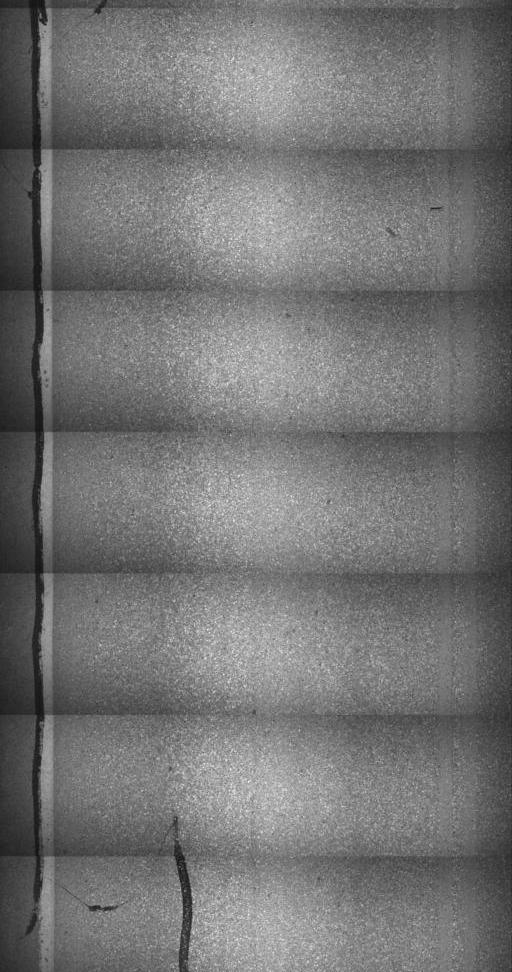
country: US
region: Vermont
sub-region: Franklin County
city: Enosburg Falls
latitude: 44.8541
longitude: -72.8034
